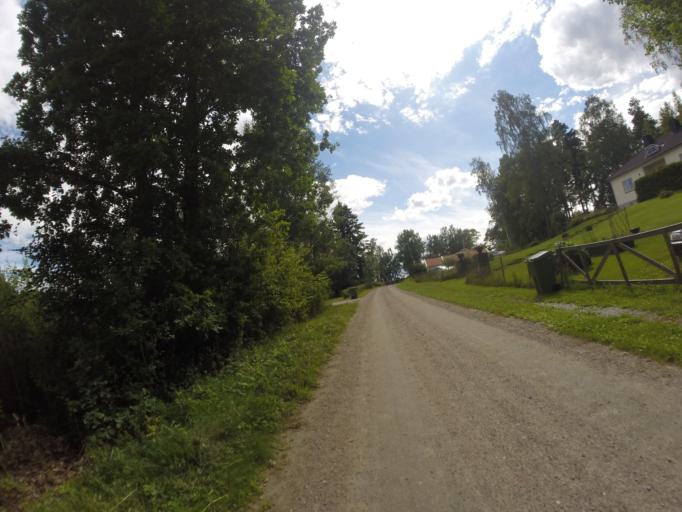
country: SE
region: Soedermanland
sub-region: Eskilstuna Kommun
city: Kvicksund
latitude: 59.4464
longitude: 16.3050
